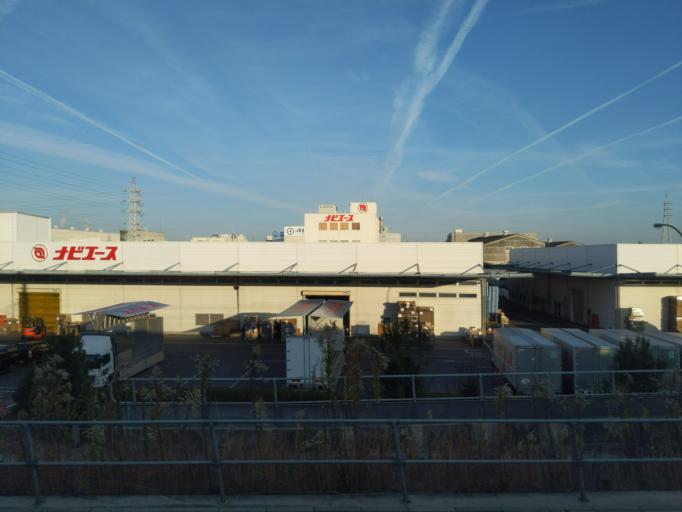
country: JP
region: Aichi
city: Kasugai
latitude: 35.2197
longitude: 136.9525
